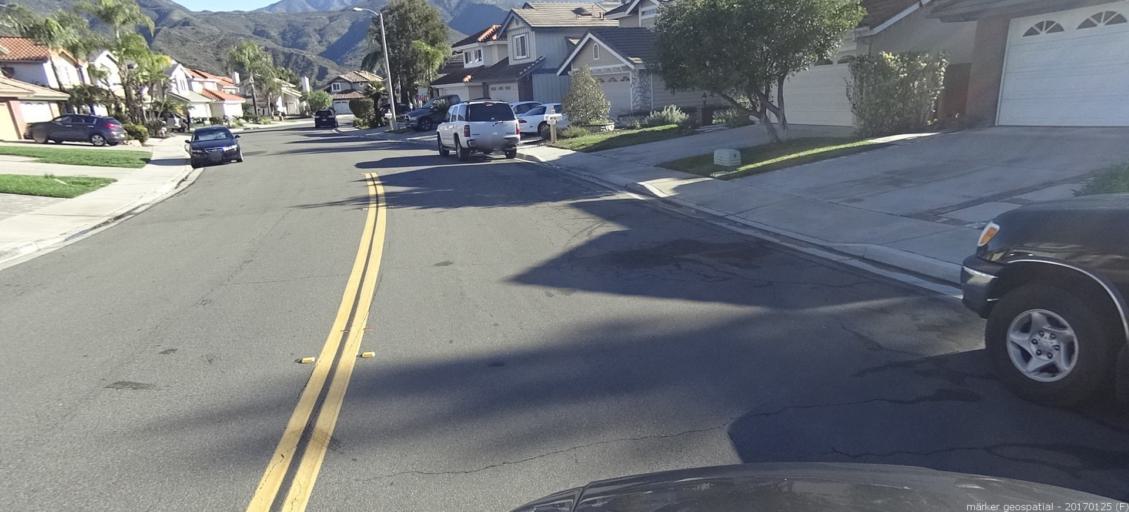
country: US
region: California
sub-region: Orange County
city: Portola Hills
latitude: 33.6876
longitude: -117.6290
